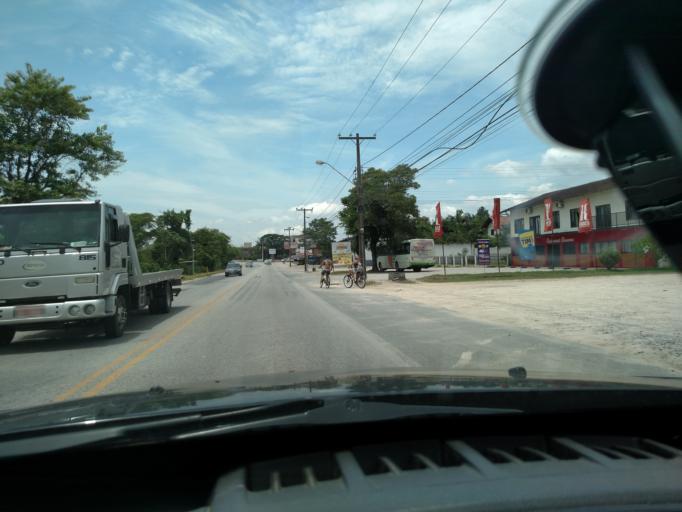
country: BR
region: Santa Catarina
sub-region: Gaspar
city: Gaspar
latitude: -26.9182
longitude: -48.9760
